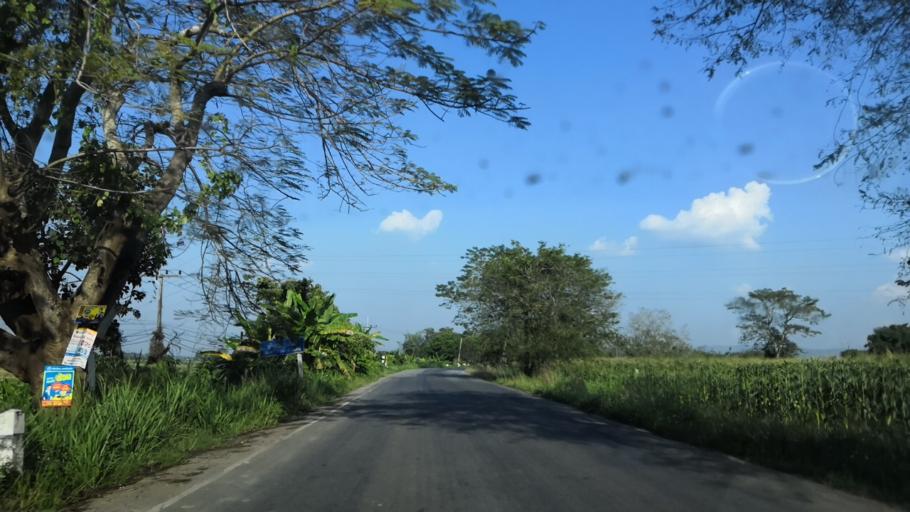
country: TH
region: Chiang Rai
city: Wiang Chai
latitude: 19.9476
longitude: 99.9205
